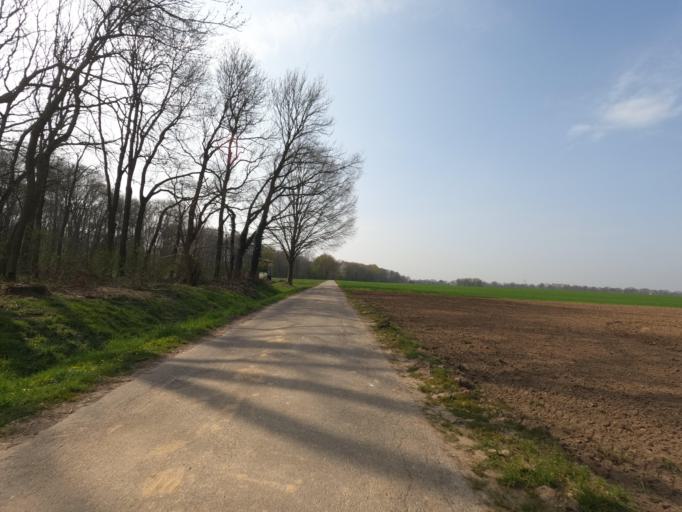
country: DE
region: North Rhine-Westphalia
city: Erkelenz
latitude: 51.0537
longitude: 6.3341
